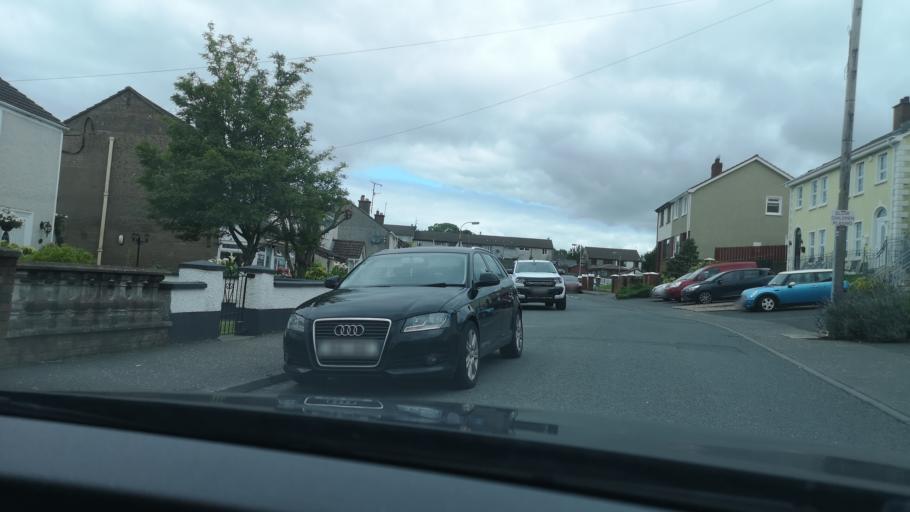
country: GB
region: Northern Ireland
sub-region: Newry and Mourne District
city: Newry
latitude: 54.1676
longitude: -6.3286
